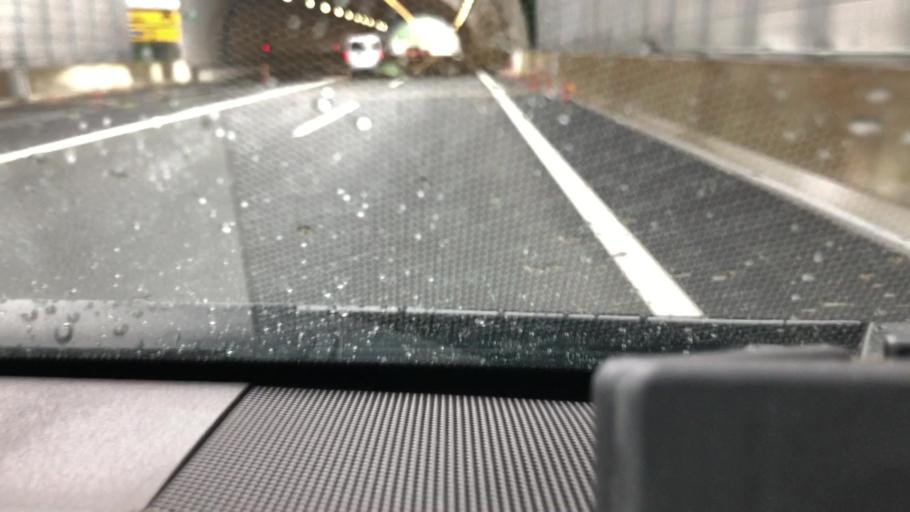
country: JP
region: Shizuoka
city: Mishima
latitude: 35.1990
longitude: 138.8885
